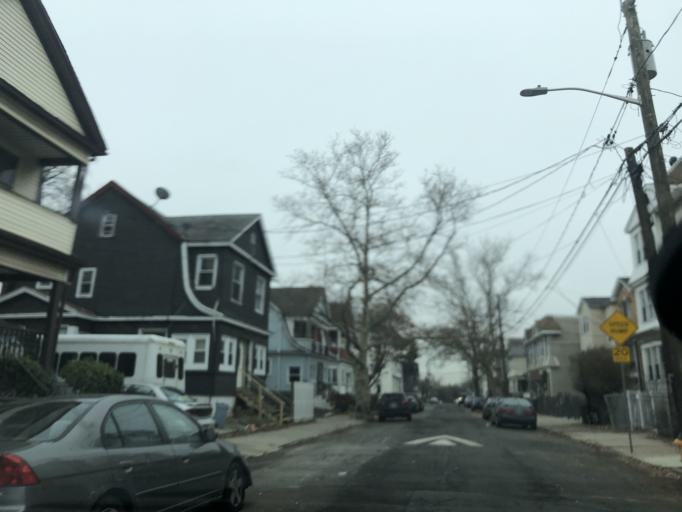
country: US
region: New Jersey
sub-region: Union County
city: Hillside
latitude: 40.7189
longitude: -74.2178
